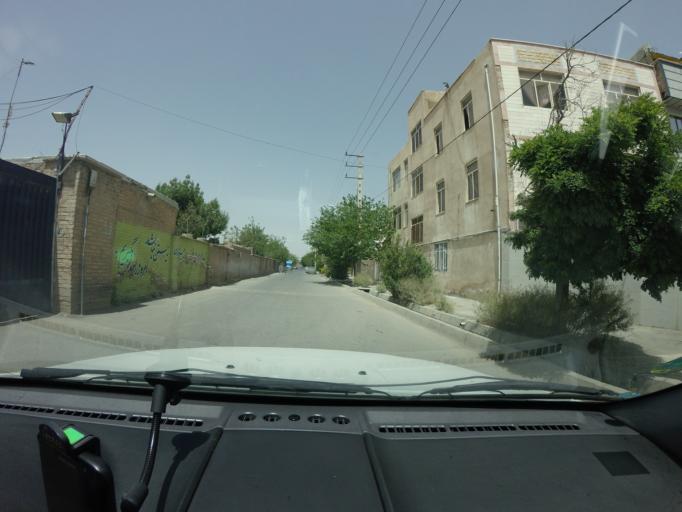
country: IR
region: Tehran
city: Eslamshahr
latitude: 35.5269
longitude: 51.2181
